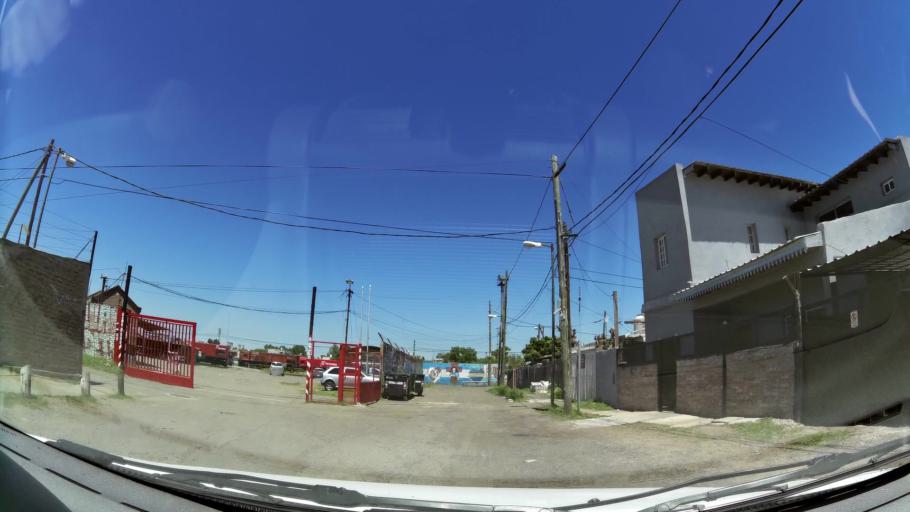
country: AR
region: Buenos Aires
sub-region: Partido de San Isidro
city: San Isidro
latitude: -34.5108
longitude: -58.5607
